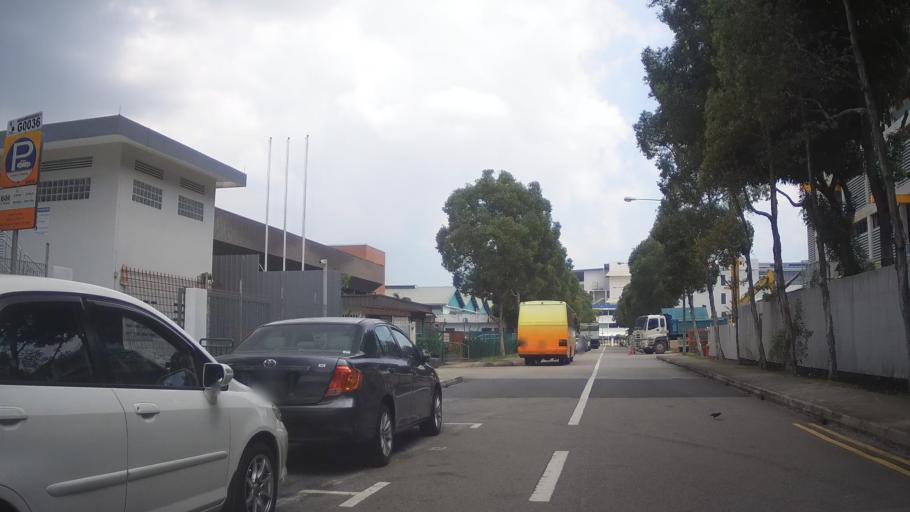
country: MY
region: Johor
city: Johor Bahru
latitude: 1.3175
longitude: 103.6630
